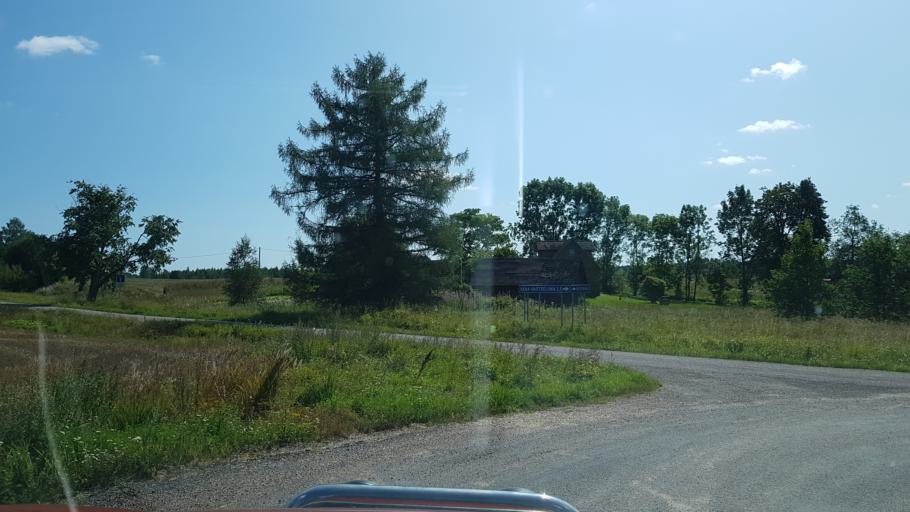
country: RU
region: Pskov
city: Pechory
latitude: 57.7091
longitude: 27.3975
